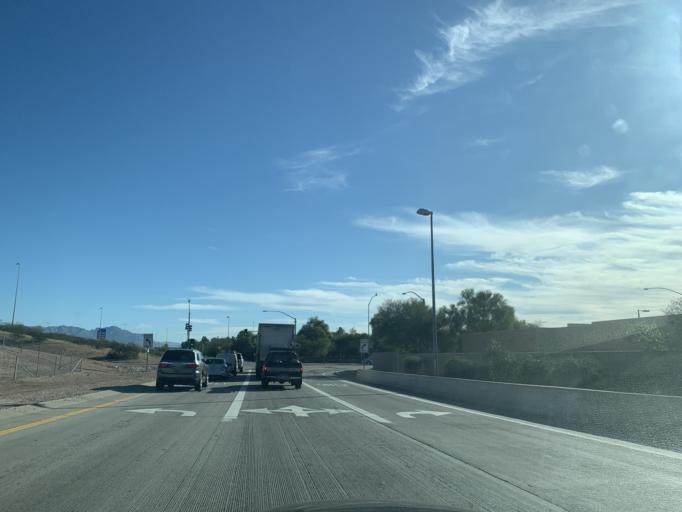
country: US
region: Arizona
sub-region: Pinal County
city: Apache Junction
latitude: 33.3860
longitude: -111.6164
